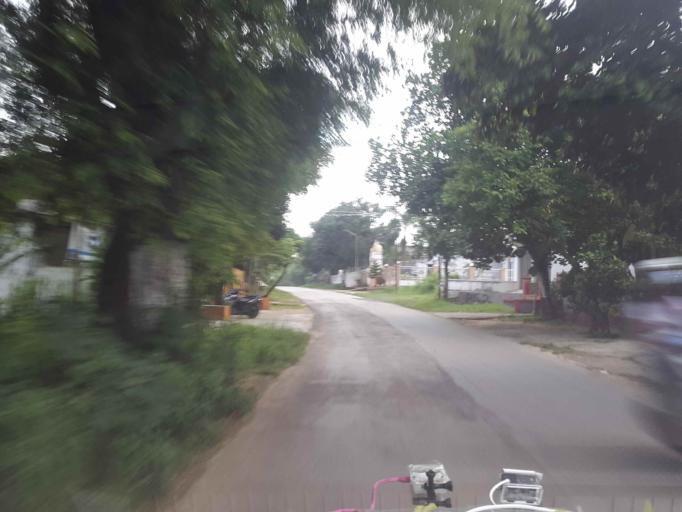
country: ID
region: East Java
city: Ganjur
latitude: -6.9746
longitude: 113.8617
